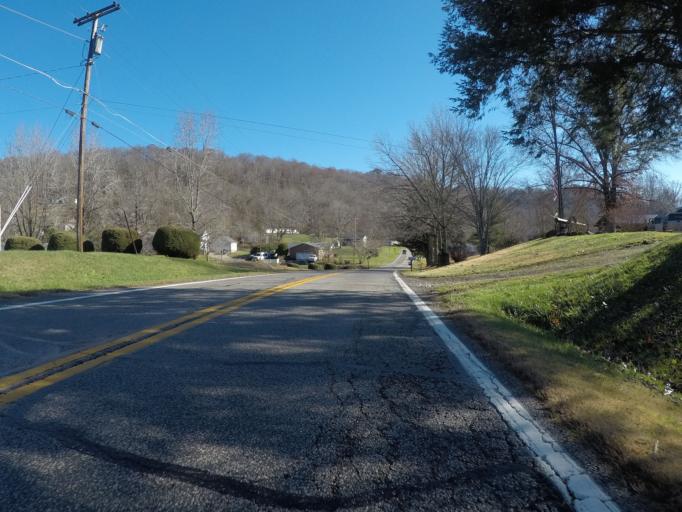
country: US
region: West Virginia
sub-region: Cabell County
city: Huntington
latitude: 38.4703
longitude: -82.4370
